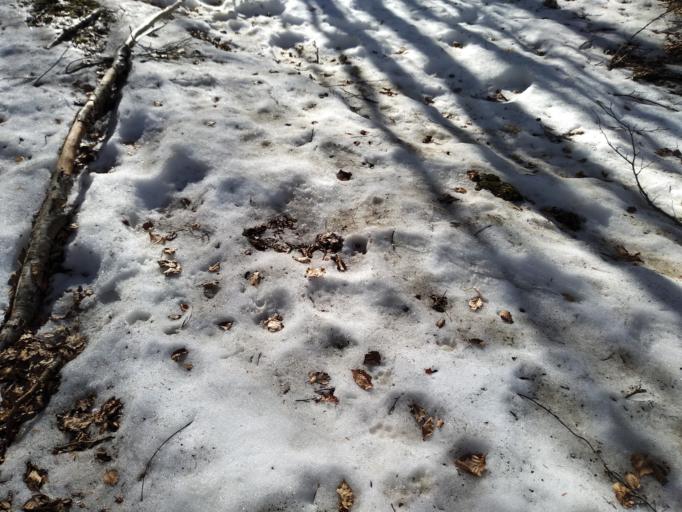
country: IT
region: Emilia-Romagna
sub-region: Provincia di Reggio Emilia
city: Collagna
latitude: 44.3782
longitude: 10.2826
